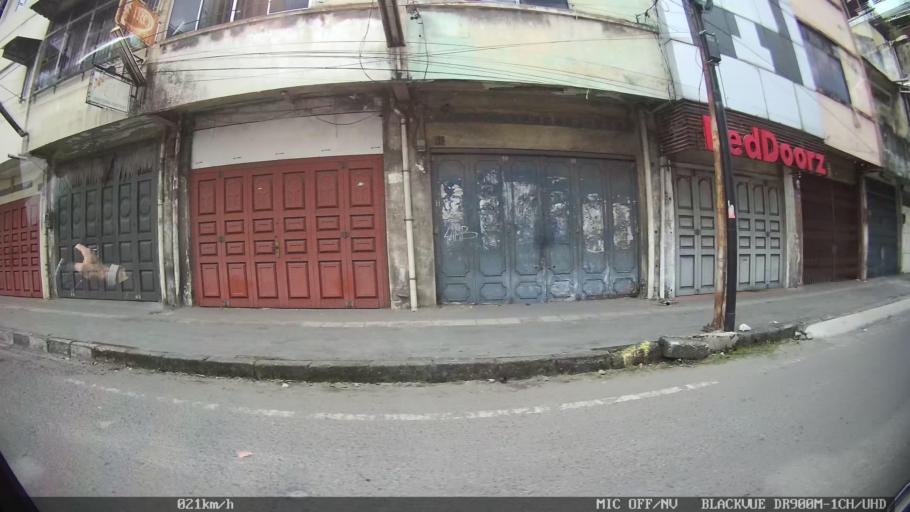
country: ID
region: North Sumatra
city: Medan
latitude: 3.5823
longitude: 98.6837
